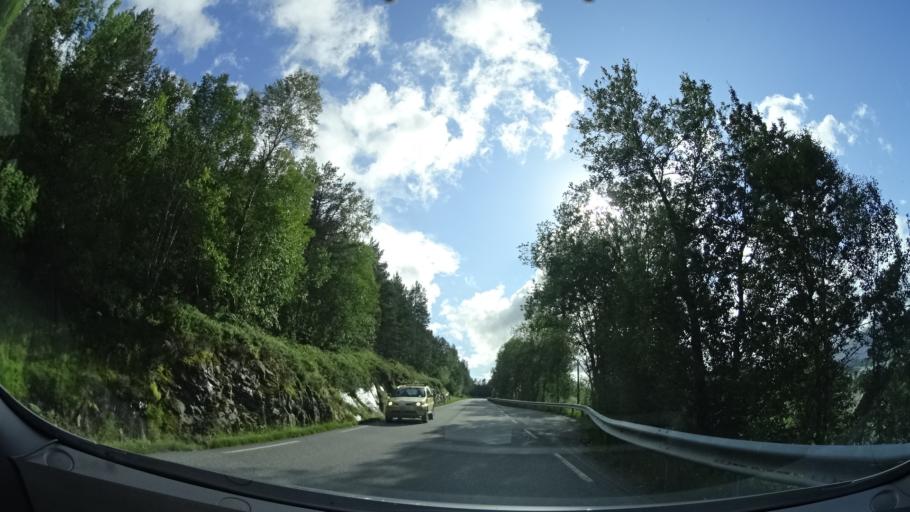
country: NO
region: More og Romsdal
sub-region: Halsa
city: Liaboen
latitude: 63.1337
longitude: 8.3932
